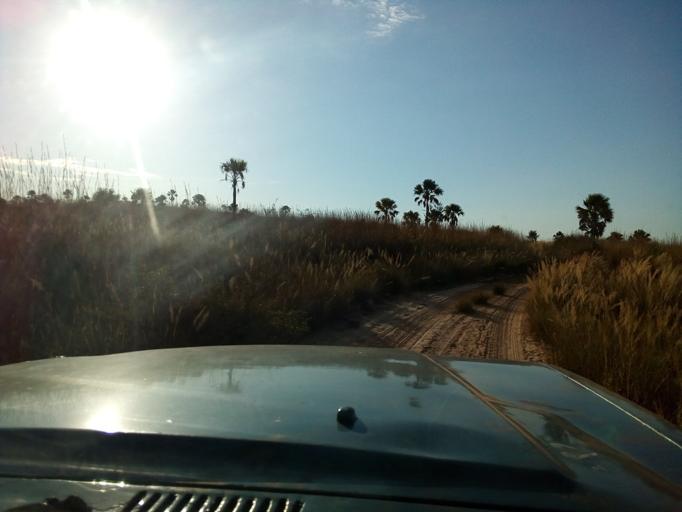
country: MG
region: Boeny
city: Sitampiky
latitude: -16.1209
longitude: 45.5250
